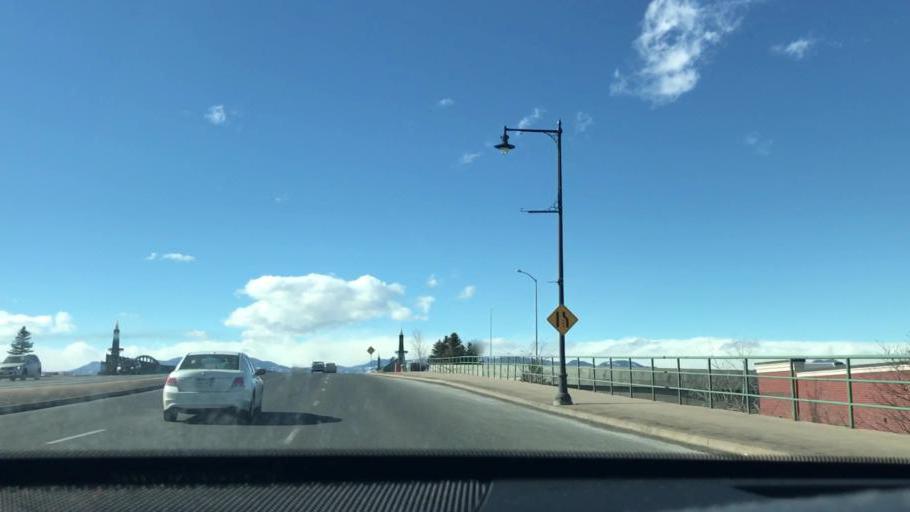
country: US
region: Colorado
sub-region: Adams County
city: Westminster
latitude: 39.8637
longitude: -105.0547
